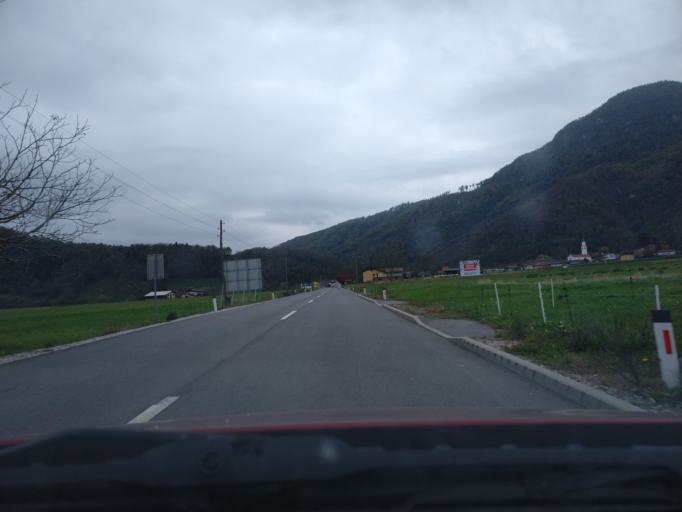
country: SI
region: Tolmin
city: Tolmin
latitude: 46.1815
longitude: 13.7121
